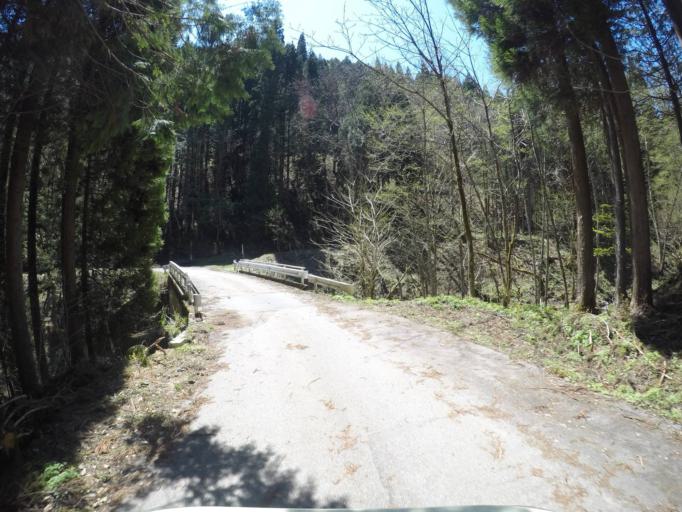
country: JP
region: Gifu
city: Takayama
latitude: 36.1565
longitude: 137.4341
